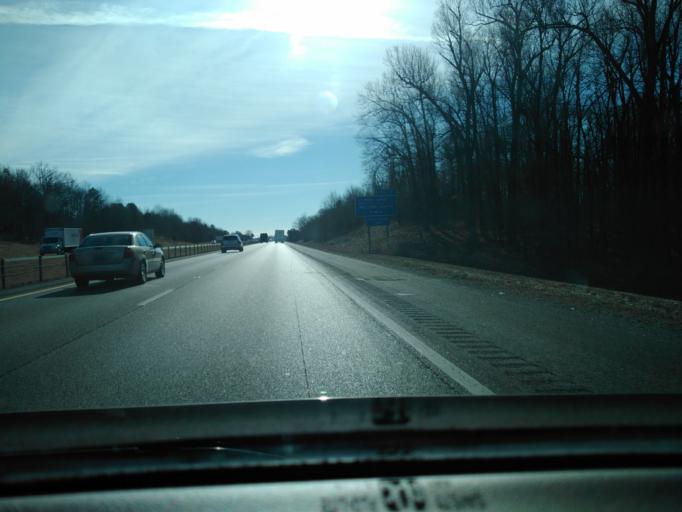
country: US
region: Kentucky
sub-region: McCracken County
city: Hendron
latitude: 37.0701
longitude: -88.6727
